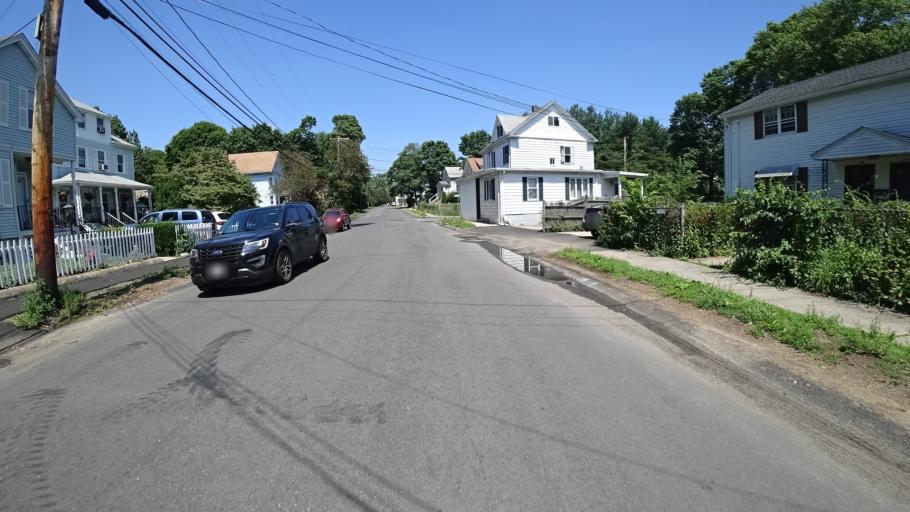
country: US
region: Massachusetts
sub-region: Norfolk County
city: Dedham
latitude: 42.2515
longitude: -71.1538
